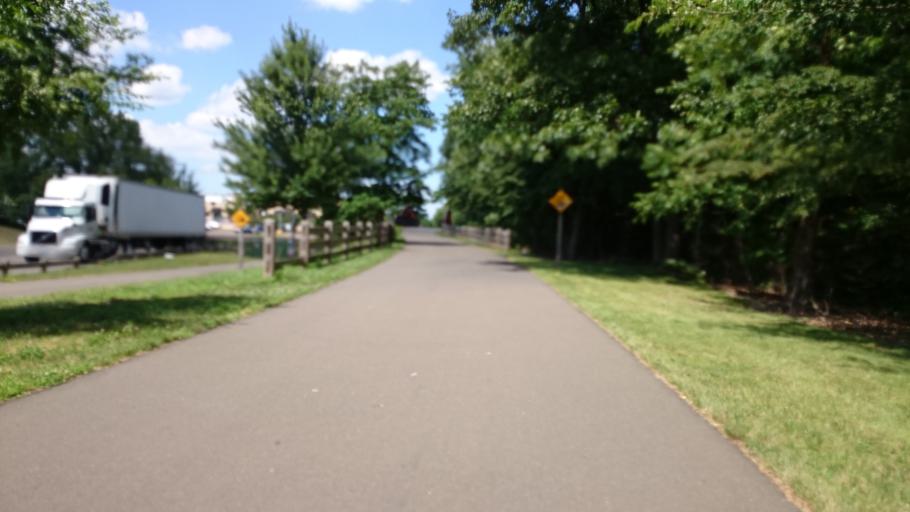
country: US
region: Connecticut
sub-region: New Haven County
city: New Haven
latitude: 41.3445
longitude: -72.9324
